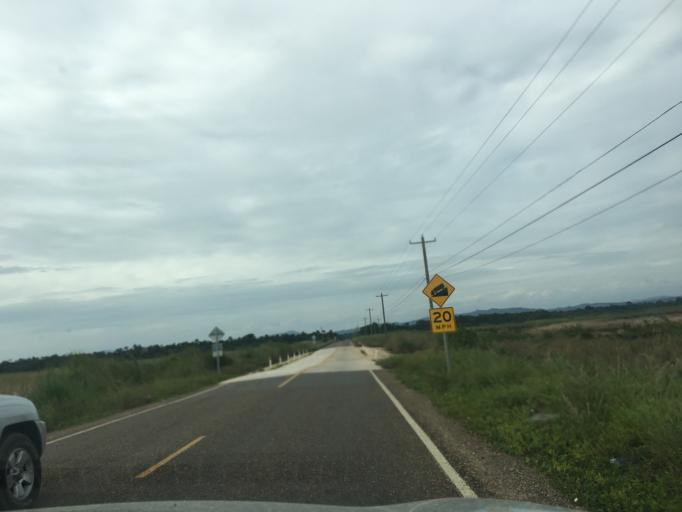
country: BZ
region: Stann Creek
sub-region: Dangriga
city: Dangriga
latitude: 16.8597
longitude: -88.2974
